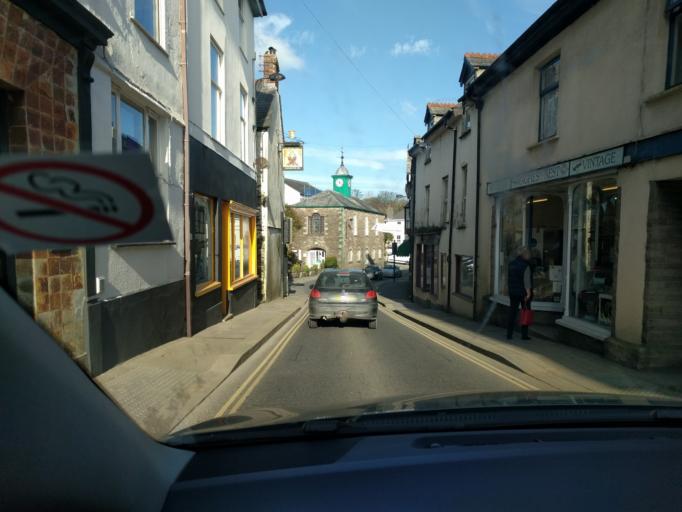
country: GB
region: England
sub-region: Cornwall
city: Camelford
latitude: 50.6219
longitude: -4.6795
